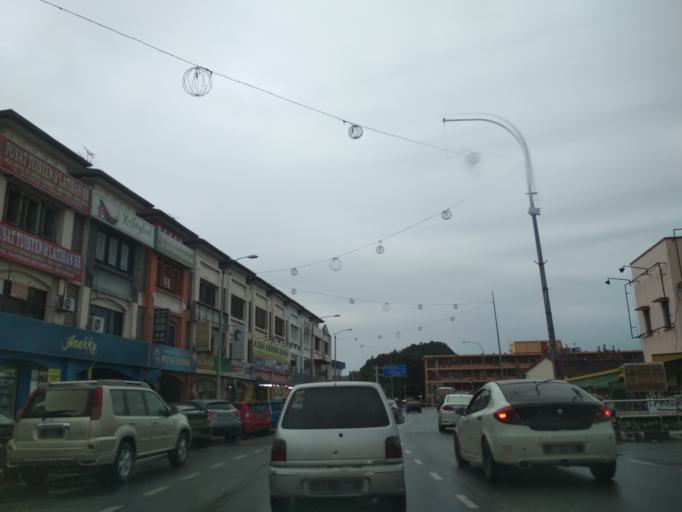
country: MY
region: Perlis
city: Kangar
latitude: 6.4382
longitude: 100.1938
